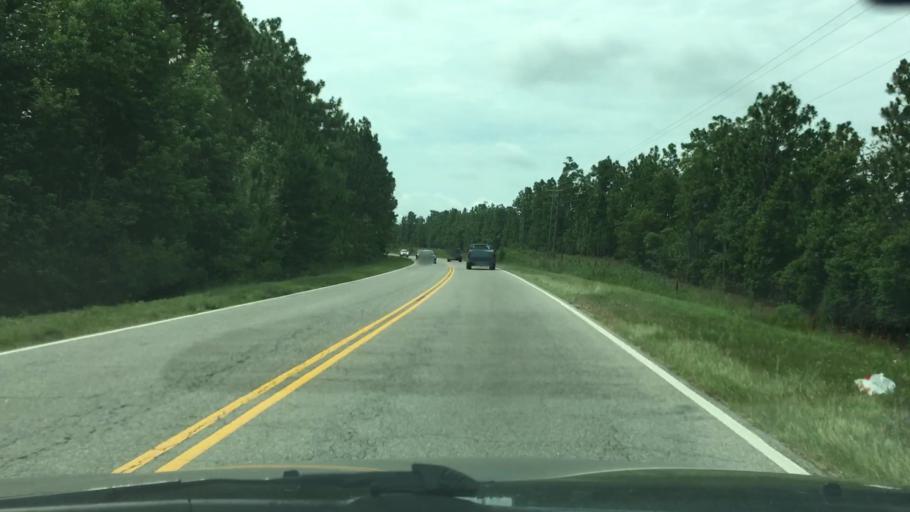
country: US
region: South Carolina
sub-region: Aiken County
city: Warrenville
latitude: 33.5360
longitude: -81.7741
